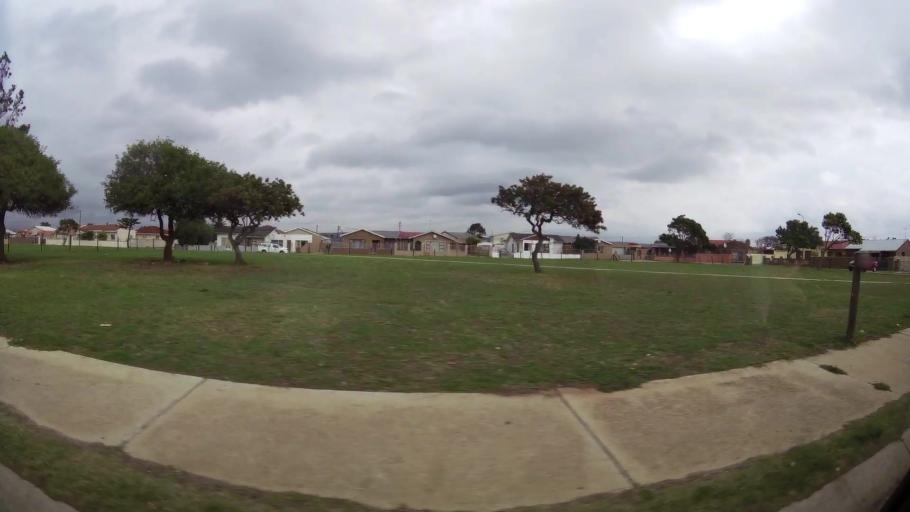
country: ZA
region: Eastern Cape
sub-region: Nelson Mandela Bay Metropolitan Municipality
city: Port Elizabeth
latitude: -33.8986
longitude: 25.5649
